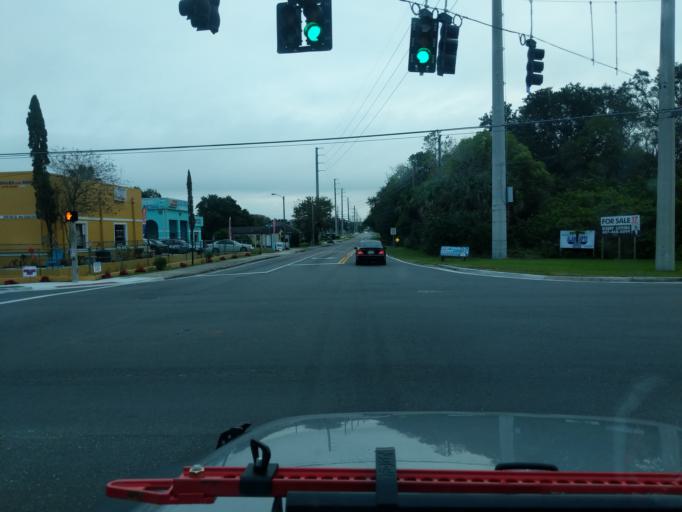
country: US
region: Florida
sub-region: Orange County
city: Winter Garden
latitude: 28.5584
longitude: -81.5754
